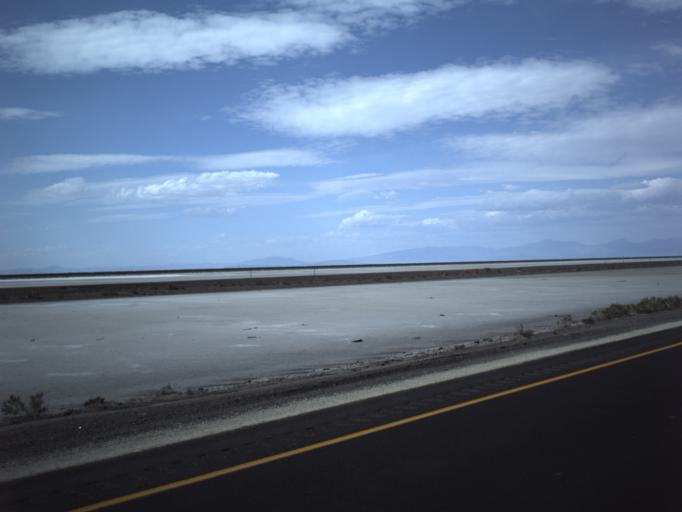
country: US
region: Utah
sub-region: Tooele County
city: Wendover
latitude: 40.7338
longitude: -113.5850
